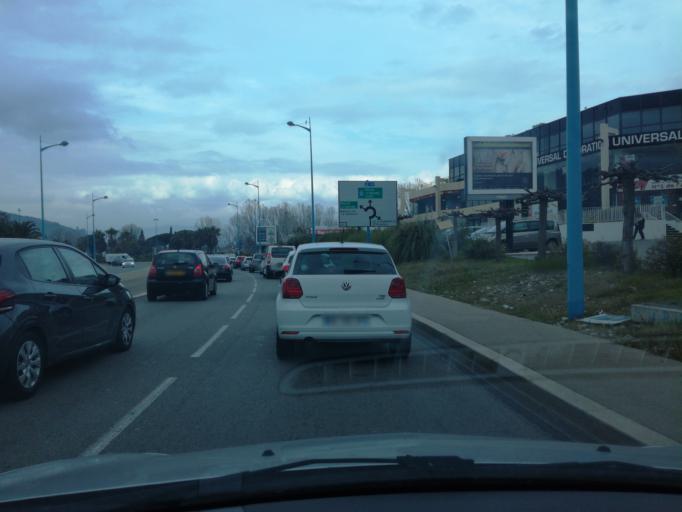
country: FR
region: Provence-Alpes-Cote d'Azur
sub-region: Departement des Alpes-Maritimes
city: Mandelieu-la-Napoule
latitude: 43.5555
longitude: 6.9542
